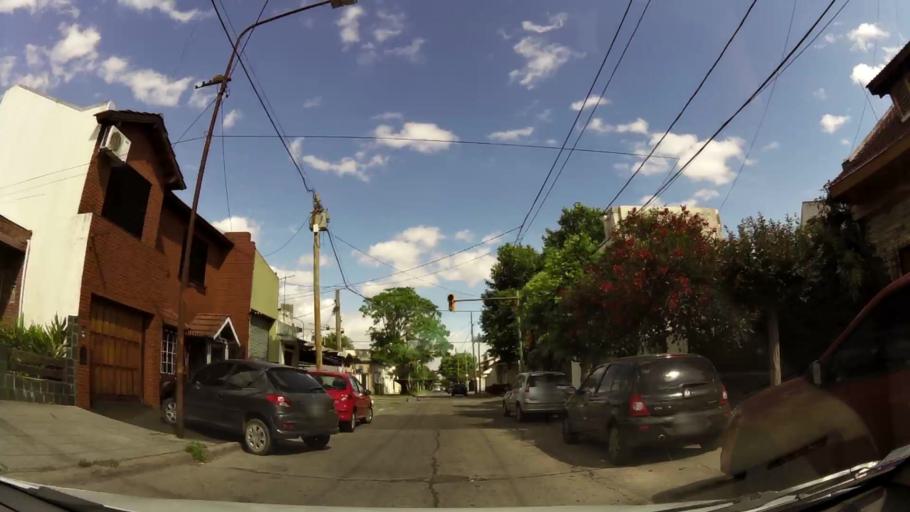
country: AR
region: Buenos Aires
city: San Justo
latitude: -34.6419
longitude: -58.5538
